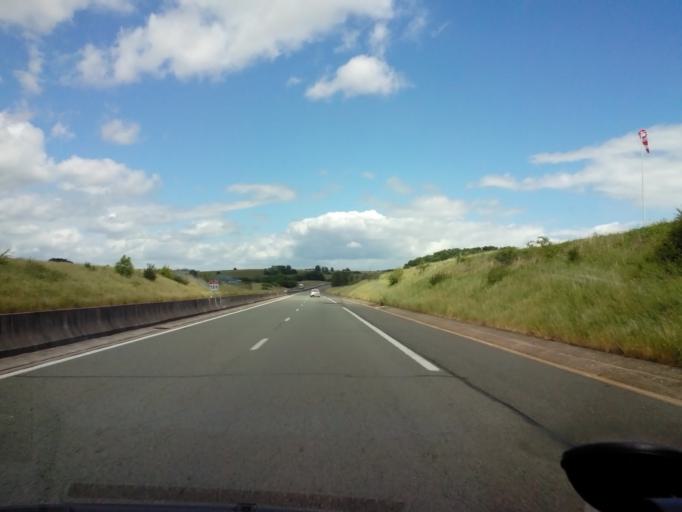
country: FR
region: Lorraine
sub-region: Departement des Vosges
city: Lamarche
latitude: 48.0926
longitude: 5.6396
